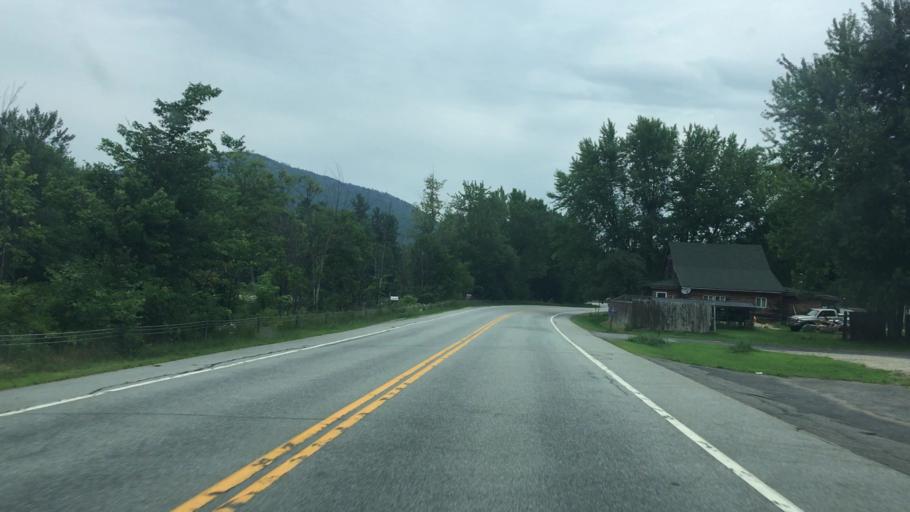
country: US
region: New York
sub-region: Essex County
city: Lake Placid
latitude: 44.3260
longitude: -73.7748
